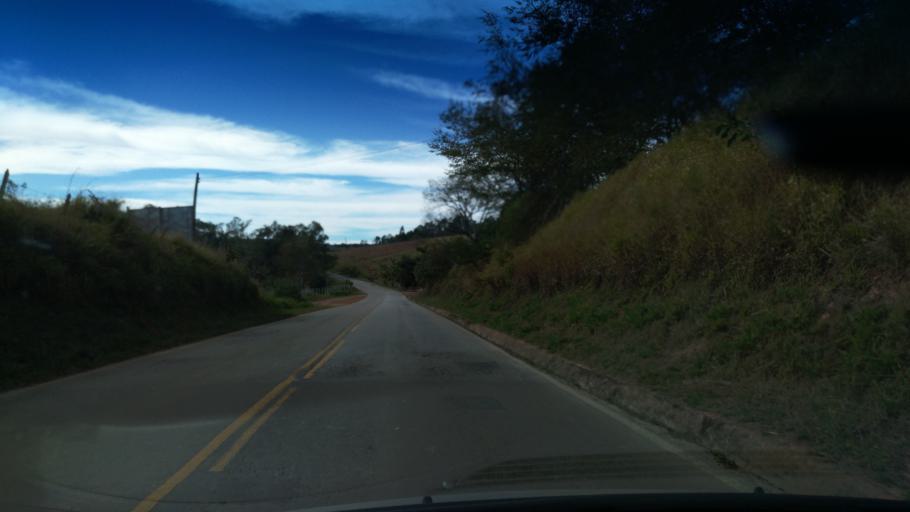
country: BR
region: Minas Gerais
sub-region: Andradas
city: Andradas
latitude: -22.0566
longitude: -46.4232
